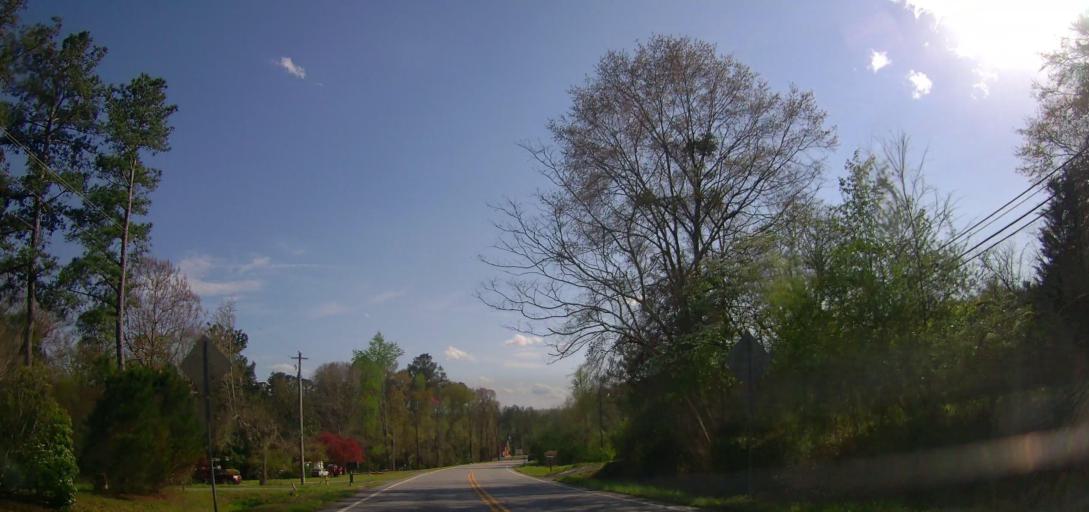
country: US
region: Georgia
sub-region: Baldwin County
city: Hardwick
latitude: 33.0433
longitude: -83.2326
